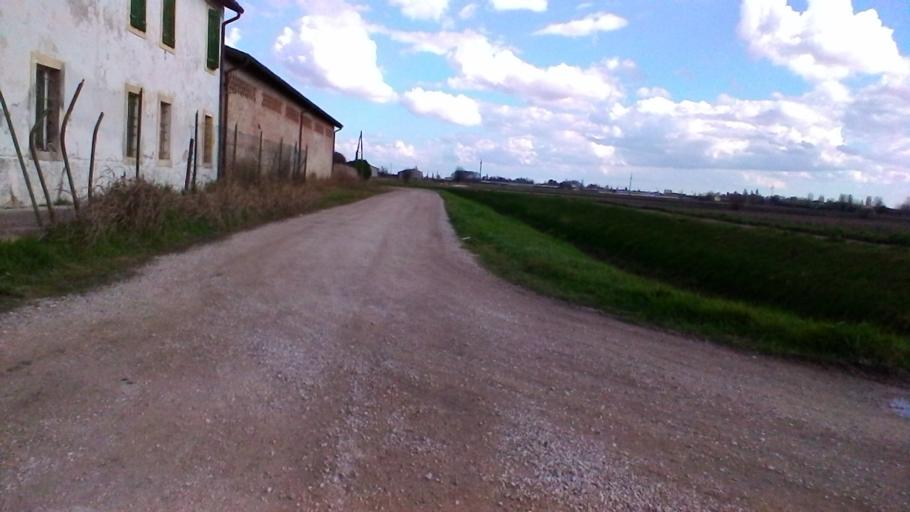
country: IT
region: Veneto
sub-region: Provincia di Verona
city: Povegliano Veronese
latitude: 45.3462
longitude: 10.9053
